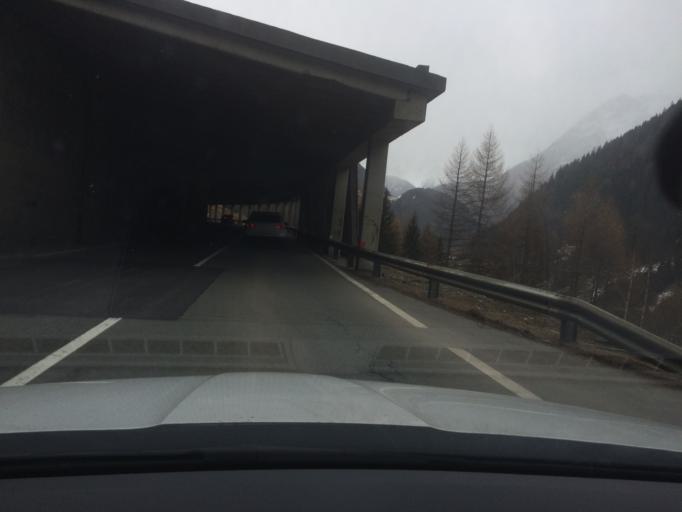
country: AT
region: Tyrol
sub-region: Politischer Bezirk Lienz
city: Matrei in Osttirol
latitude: 47.0776
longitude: 12.5309
